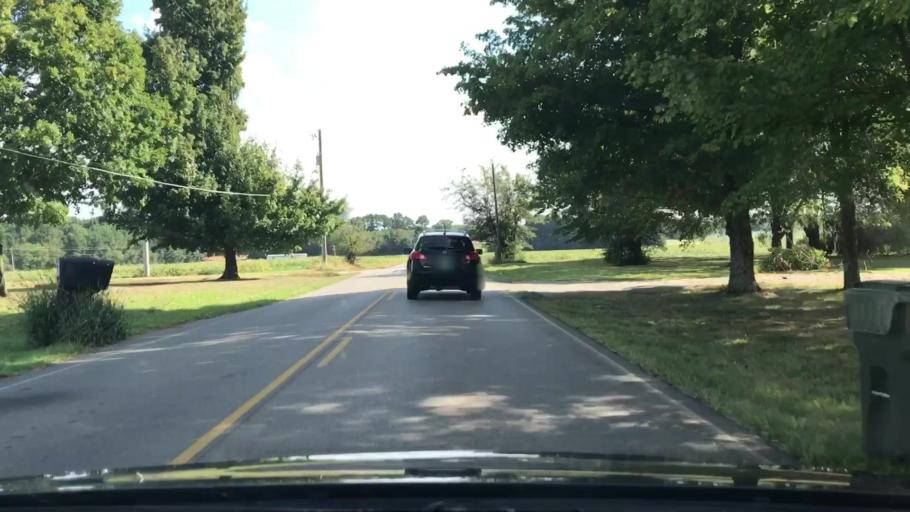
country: US
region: Alabama
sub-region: Madison County
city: Harvest
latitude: 34.8678
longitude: -86.7488
